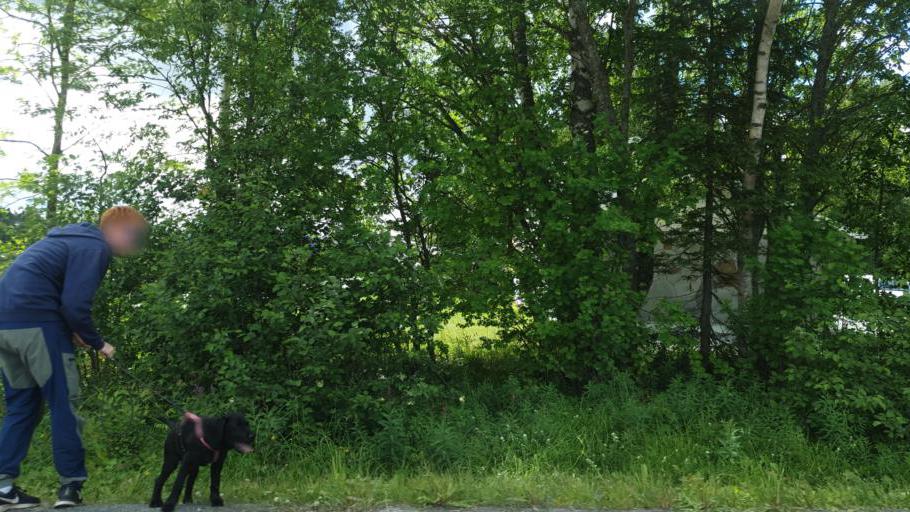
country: NO
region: Sor-Trondelag
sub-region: Rennebu
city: Berkak
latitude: 62.8325
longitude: 10.0096
